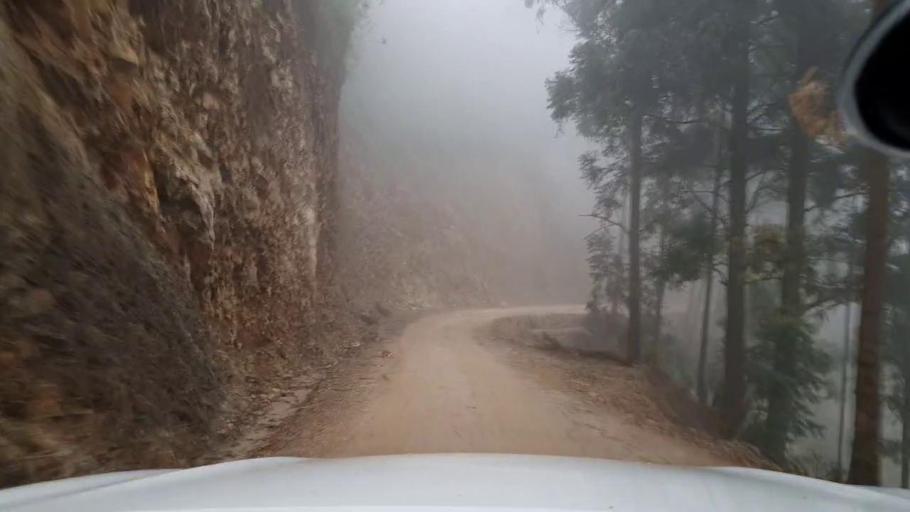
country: RW
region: Western Province
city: Cyangugu
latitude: -2.5902
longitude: 29.1904
